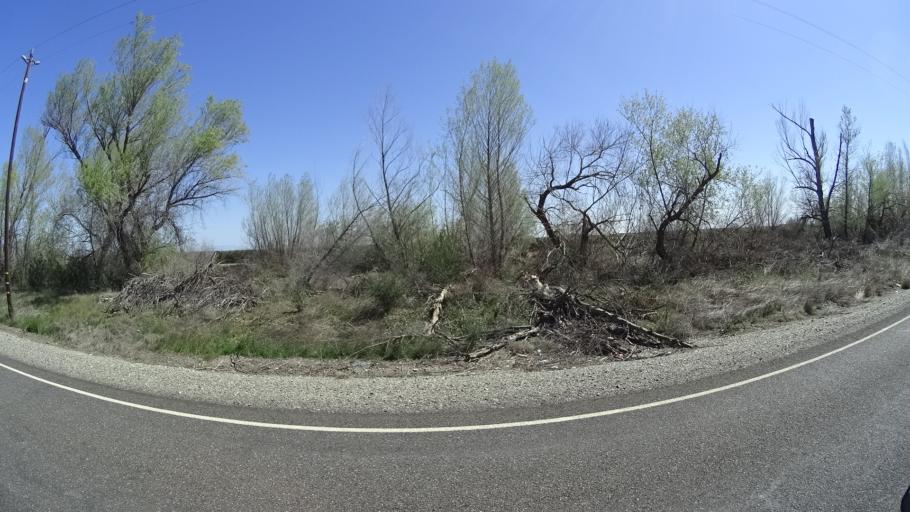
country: US
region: California
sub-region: Glenn County
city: Willows
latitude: 39.6159
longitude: -122.2500
